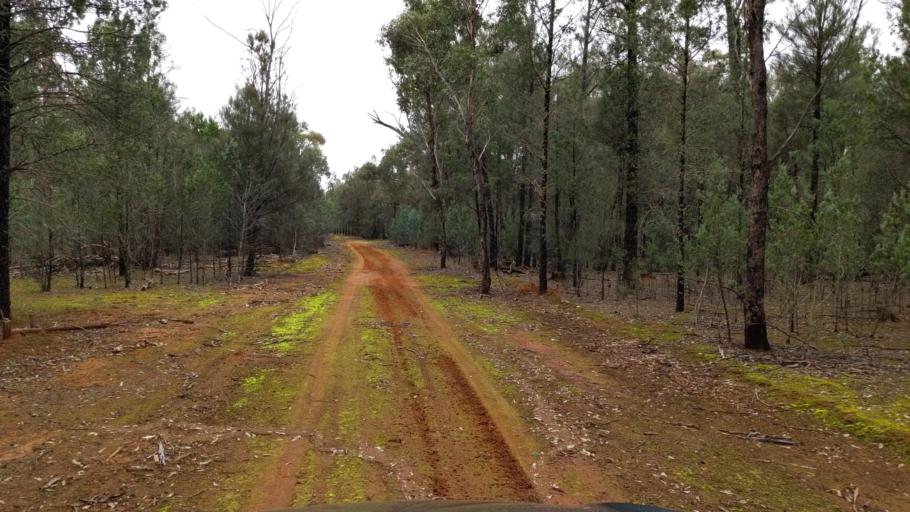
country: AU
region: New South Wales
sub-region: Coolamon
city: Coolamon
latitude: -34.8300
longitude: 146.9355
